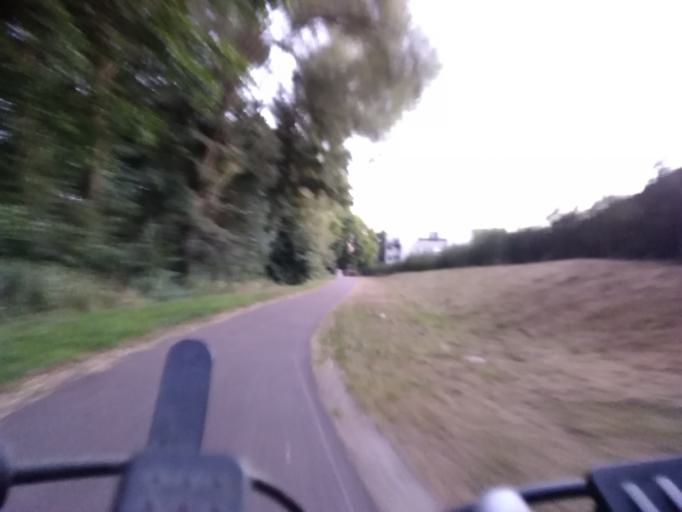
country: FR
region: Lorraine
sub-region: Departement de la Moselle
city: Neufgrange
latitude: 49.0784
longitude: 7.0596
